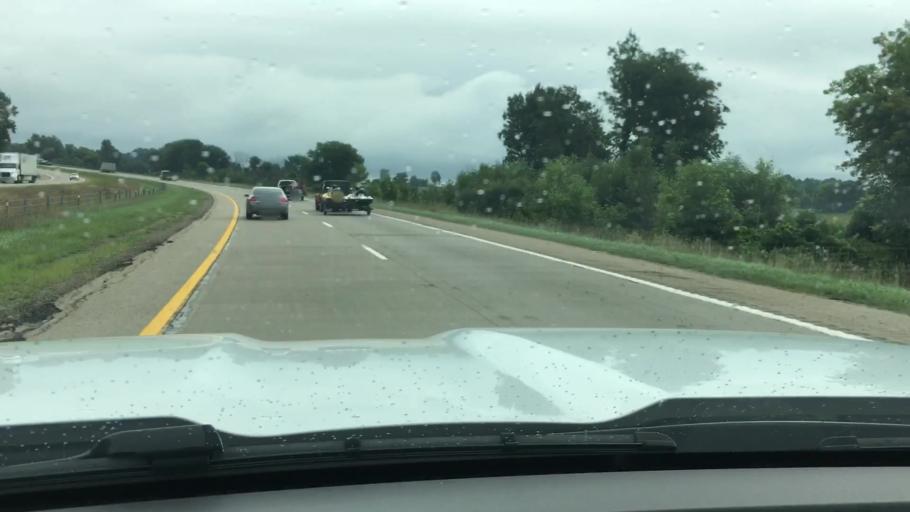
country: US
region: Michigan
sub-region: Kent County
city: Lowell
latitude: 42.8741
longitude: -85.3211
